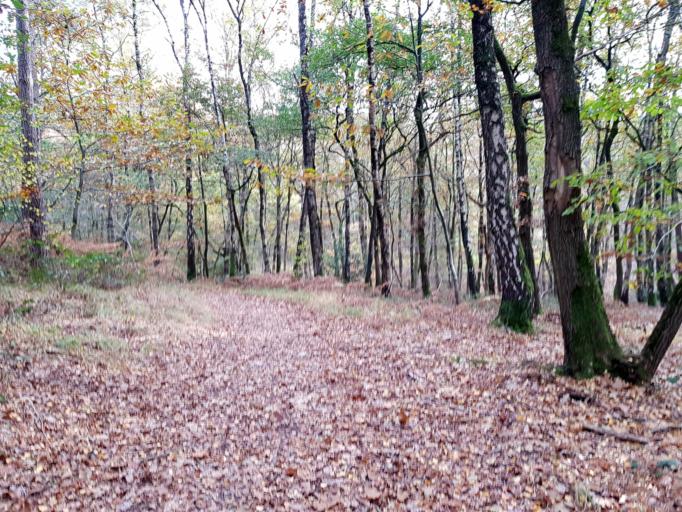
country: NL
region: Gelderland
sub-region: Gemeente Groesbeek
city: Bredeweg
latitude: 51.7446
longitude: 5.9258
